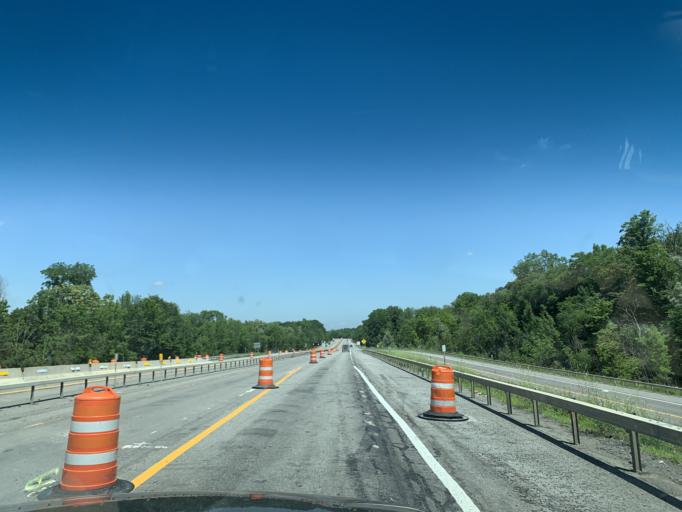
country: US
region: New York
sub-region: Oneida County
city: Chadwicks
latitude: 43.0060
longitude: -75.2537
